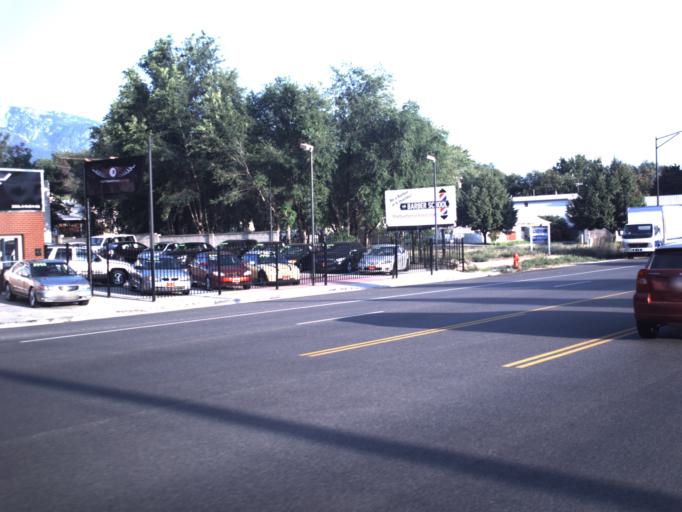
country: US
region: Utah
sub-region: Salt Lake County
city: Sandy City
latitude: 40.5917
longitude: -111.8910
